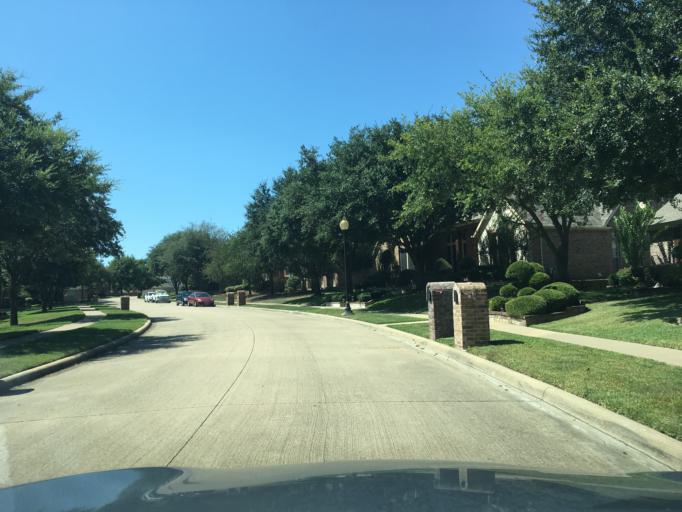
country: US
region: Texas
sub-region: Dallas County
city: Sachse
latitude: 32.9608
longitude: -96.6213
